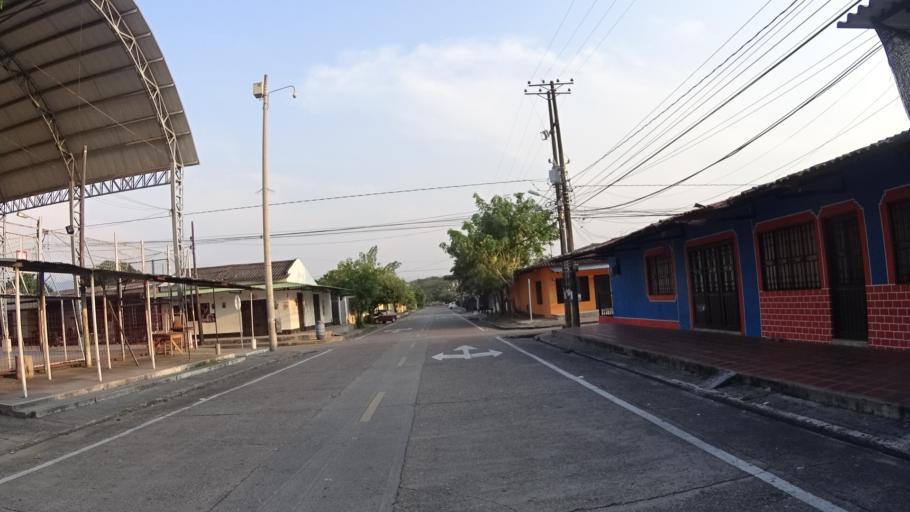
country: CO
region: Cundinamarca
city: Puerto Salgar
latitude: 5.4813
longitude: -74.6707
